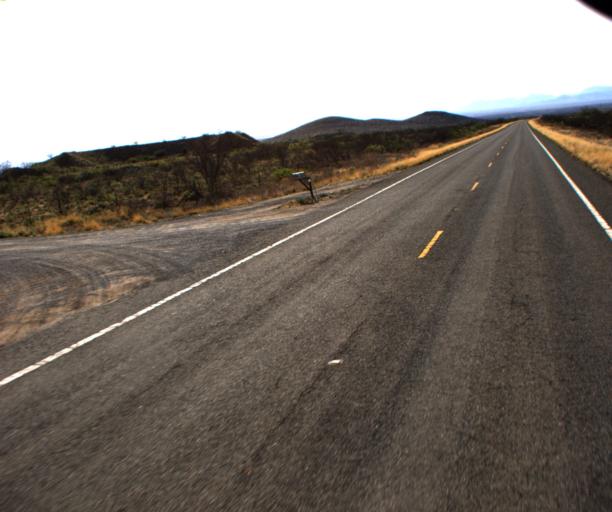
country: US
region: Arizona
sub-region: Cochise County
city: Willcox
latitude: 32.1831
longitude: -109.6660
